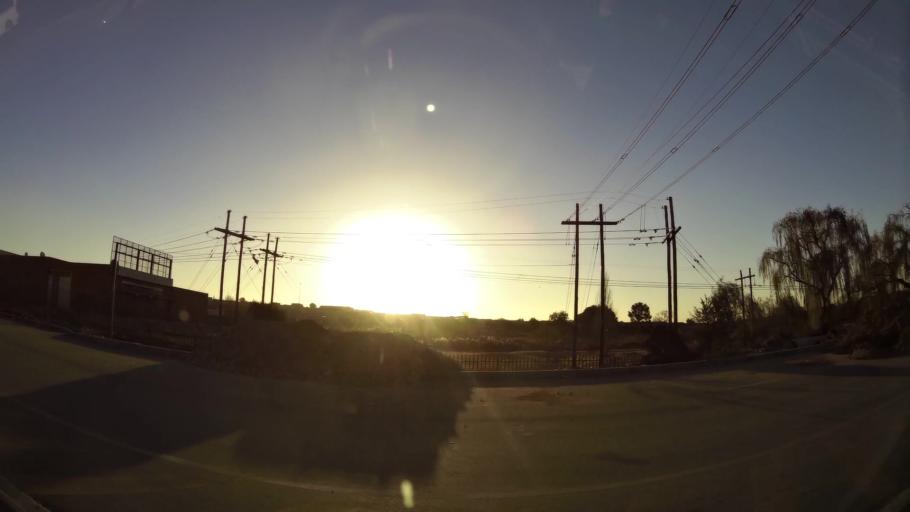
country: ZA
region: Gauteng
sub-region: Ekurhuleni Metropolitan Municipality
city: Tembisa
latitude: -26.0175
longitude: 28.2022
